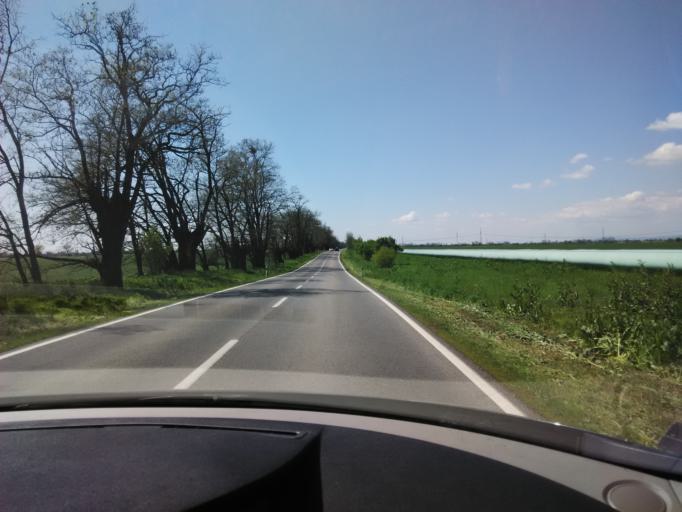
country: SK
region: Trnavsky
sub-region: Okres Trnava
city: Trnava
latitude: 48.4393
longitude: 17.6563
